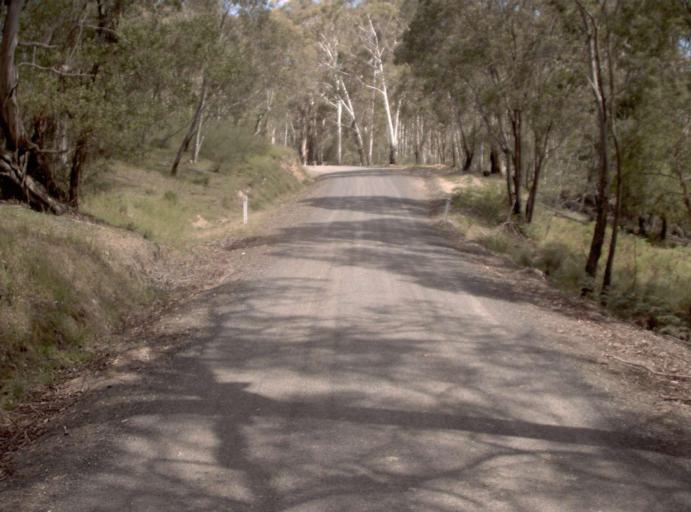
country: AU
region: New South Wales
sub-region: Bombala
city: Bombala
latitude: -37.1558
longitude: 148.6746
